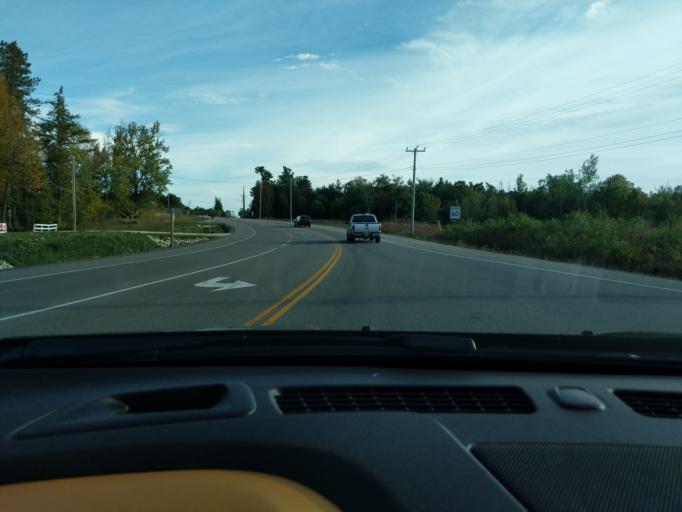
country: CA
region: Ontario
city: Barrie
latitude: 44.4272
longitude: -79.7647
